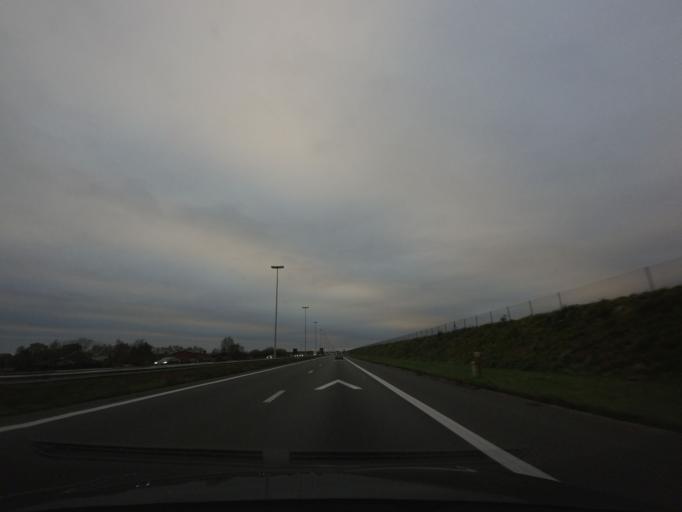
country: BE
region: Flanders
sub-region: Provincie Antwerpen
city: Hoogstraten
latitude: 51.4425
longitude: 4.7163
